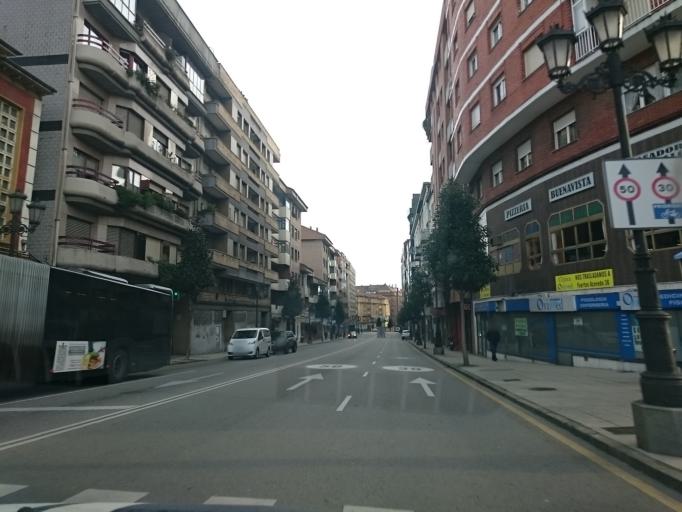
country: ES
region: Asturias
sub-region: Province of Asturias
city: Oviedo
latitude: 43.3662
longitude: -5.8558
